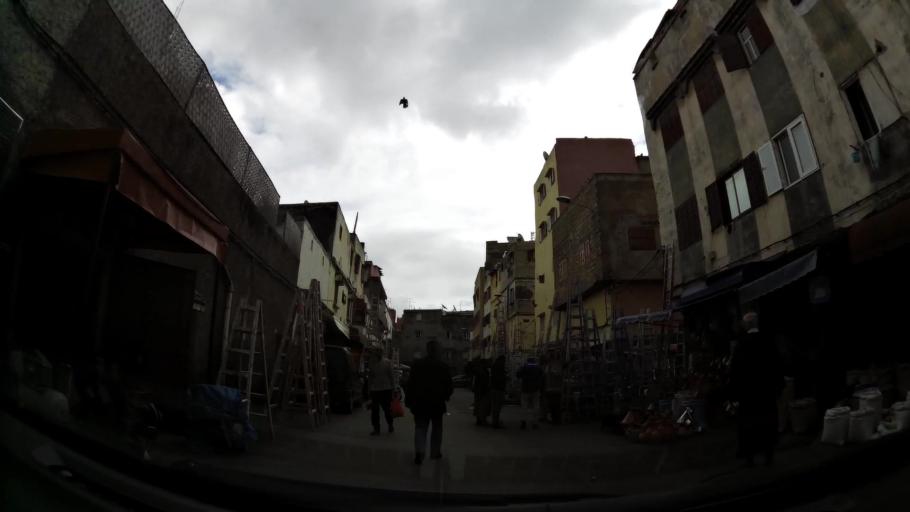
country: MA
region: Grand Casablanca
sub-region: Casablanca
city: Casablanca
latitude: 33.5757
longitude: -7.6310
